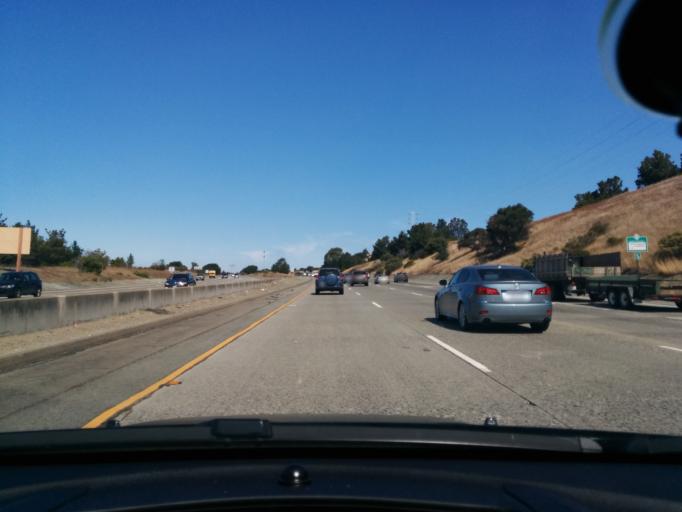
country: US
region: California
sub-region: San Mateo County
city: Highlands-Baywood Park
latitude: 37.5335
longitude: -122.3620
